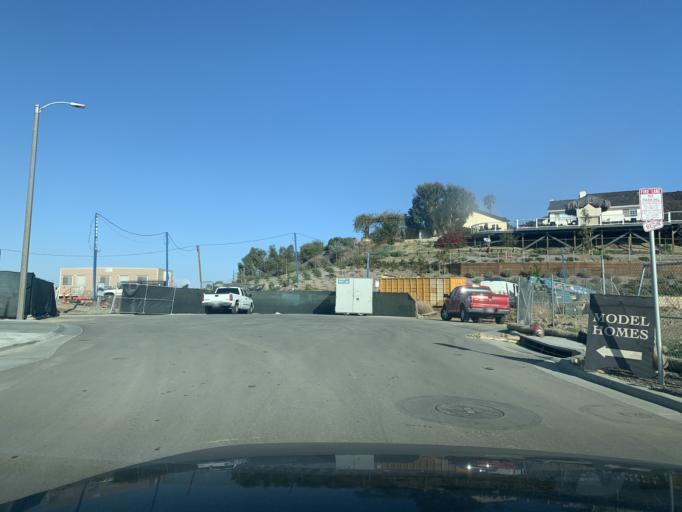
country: US
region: California
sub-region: Orange County
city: Villa Park
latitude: 33.8305
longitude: -117.8247
